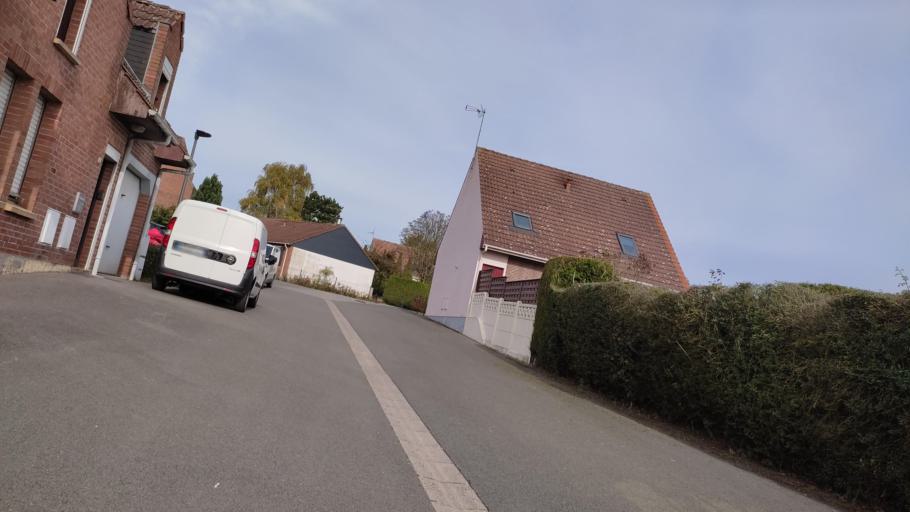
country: FR
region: Nord-Pas-de-Calais
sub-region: Departement du Pas-de-Calais
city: Feuchy
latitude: 50.3047
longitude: 2.8373
